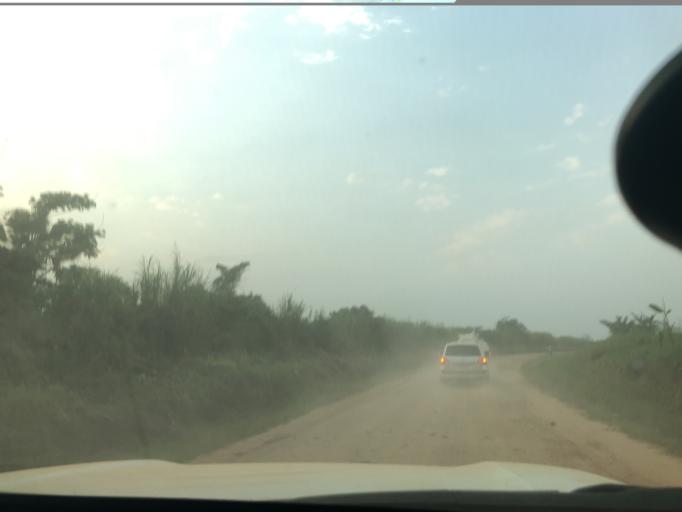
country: CD
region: Nord Kivu
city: Beni
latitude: 0.3786
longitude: 29.5996
